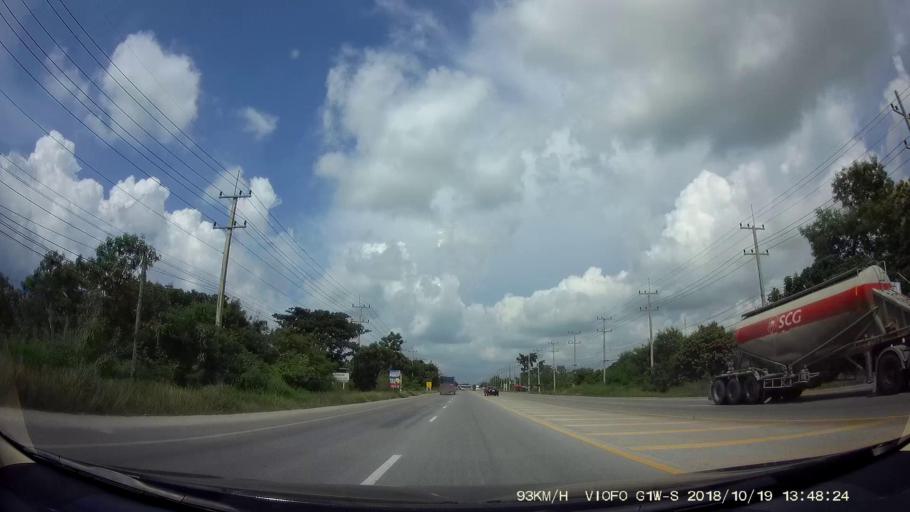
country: TH
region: Chaiyaphum
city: Chaiyaphum
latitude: 15.7256
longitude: 102.0192
